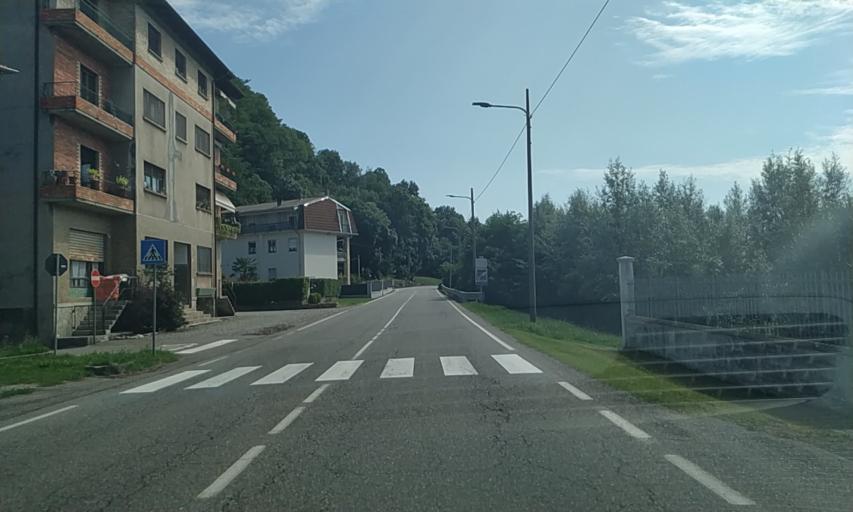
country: IT
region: Piedmont
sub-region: Provincia di Novara
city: Prato Sesia
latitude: 45.6435
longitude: 8.3750
